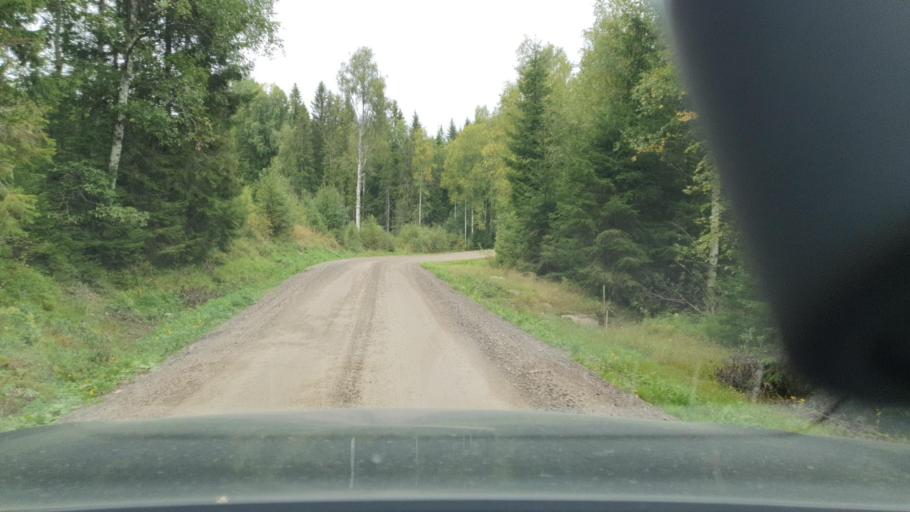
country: SE
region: Vaermland
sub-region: Eda Kommun
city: Charlottenberg
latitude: 60.0671
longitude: 12.5373
